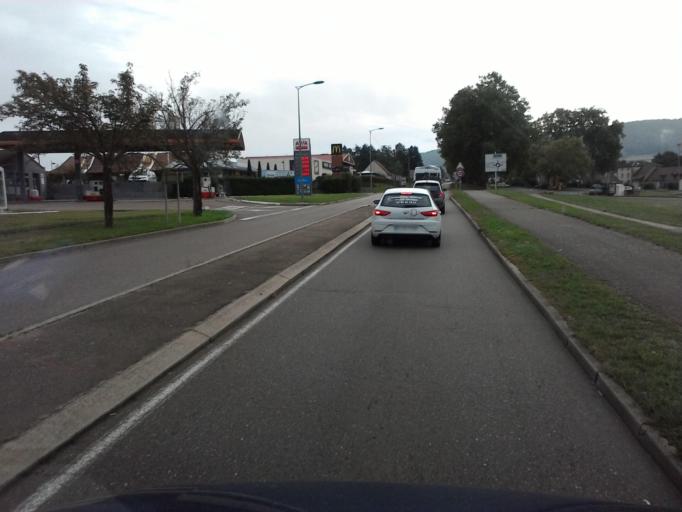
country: FR
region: Bourgogne
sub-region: Departement de Saone-et-Loire
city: Autun
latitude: 46.9562
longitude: 4.3157
